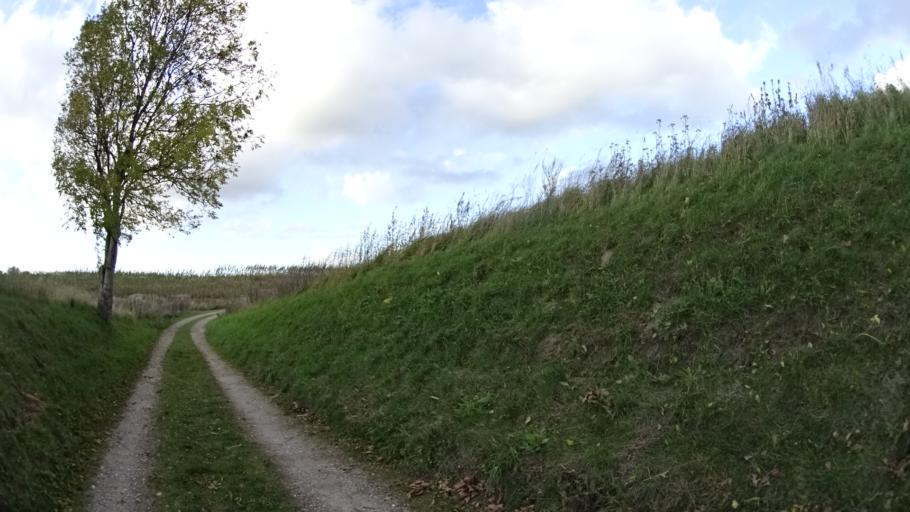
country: DK
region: Central Jutland
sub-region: Arhus Kommune
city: Kolt
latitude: 56.1263
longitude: 10.0646
